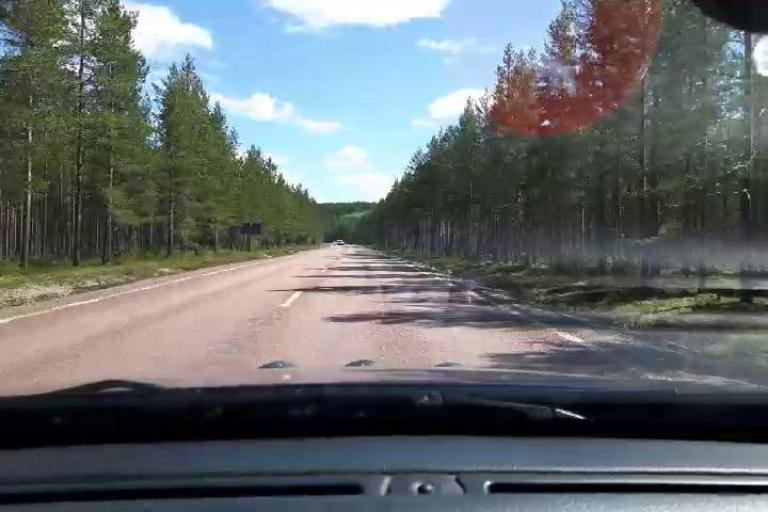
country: SE
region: Gaevleborg
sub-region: Ljusdals Kommun
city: Farila
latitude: 61.8917
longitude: 15.6645
